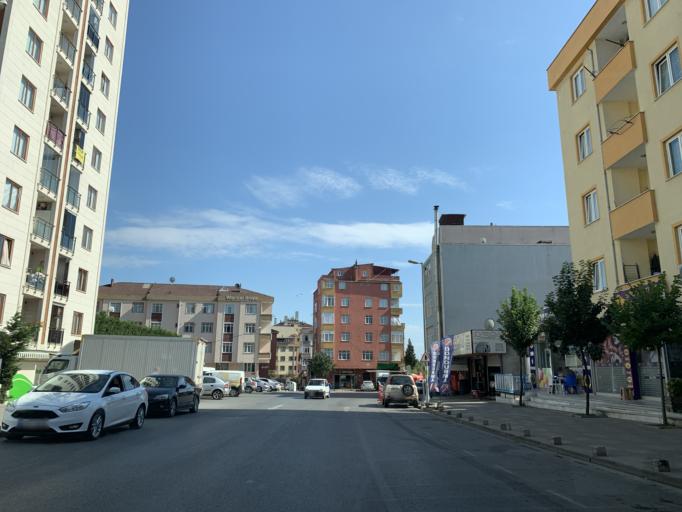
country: TR
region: Istanbul
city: Pendik
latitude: 40.8868
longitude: 29.2730
